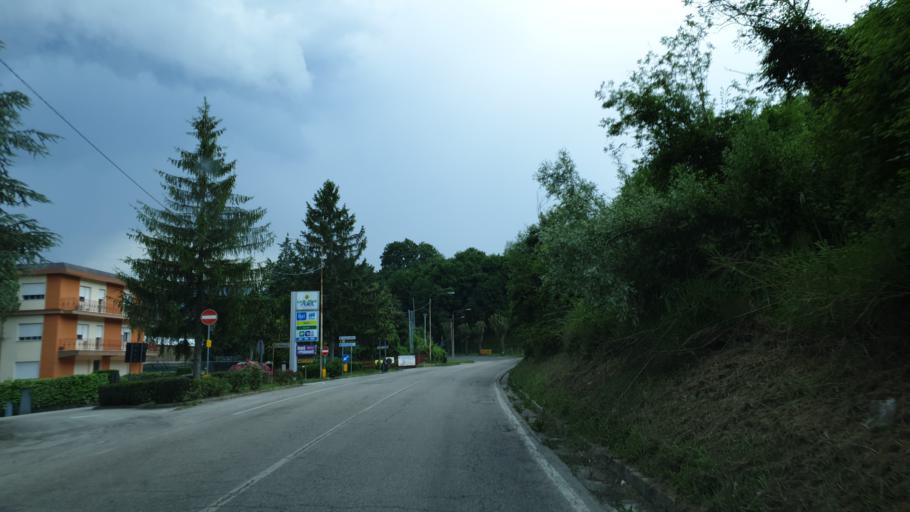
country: IT
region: Emilia-Romagna
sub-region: Provincia di Rimini
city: Talamello
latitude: 43.9059
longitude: 12.2936
